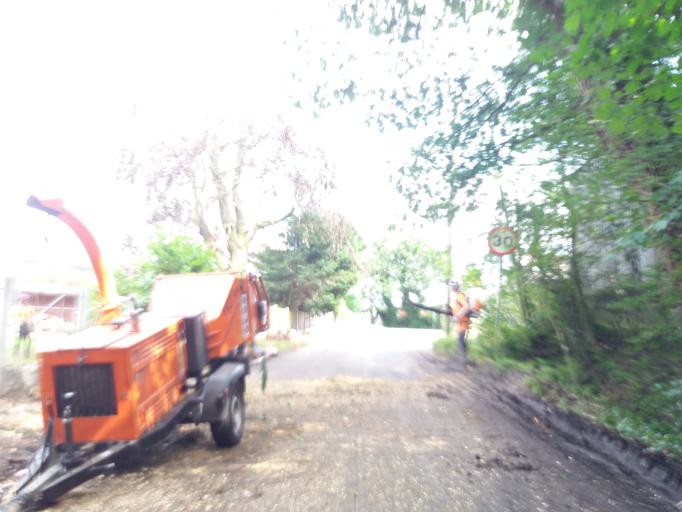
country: GB
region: England
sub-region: Lancashire
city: Euxton
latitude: 53.6638
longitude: -2.6619
